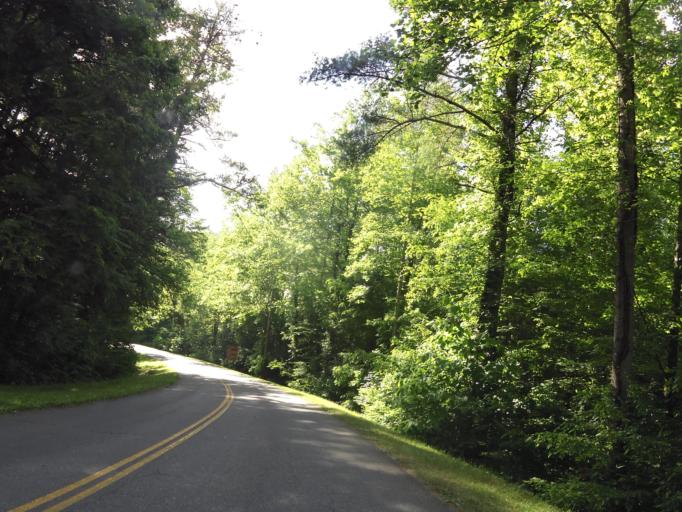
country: US
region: Tennessee
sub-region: Sevier County
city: Gatlinburg
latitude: 35.6862
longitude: -83.5392
